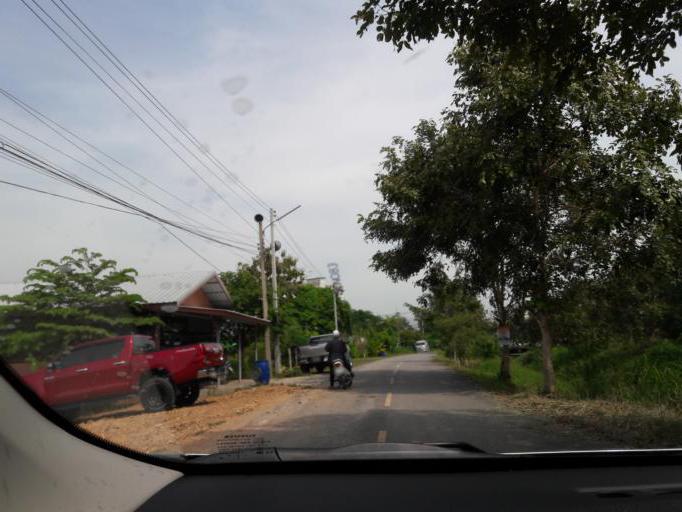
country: TH
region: Ang Thong
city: Ang Thong
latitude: 14.5838
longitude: 100.4547
